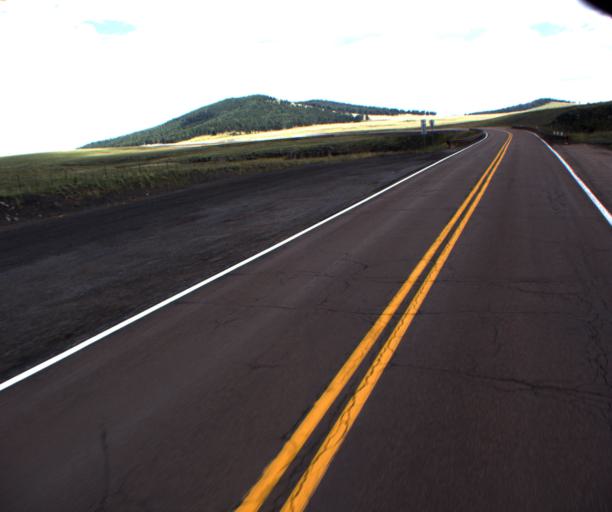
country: US
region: Arizona
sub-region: Apache County
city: Eagar
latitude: 34.0526
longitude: -109.5453
